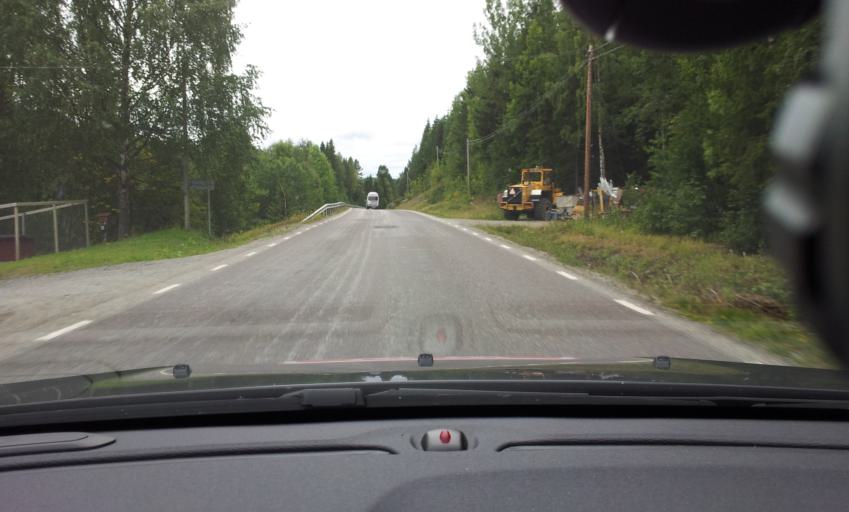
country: SE
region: Jaemtland
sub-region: Braecke Kommun
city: Braecke
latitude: 63.0297
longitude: 15.2433
